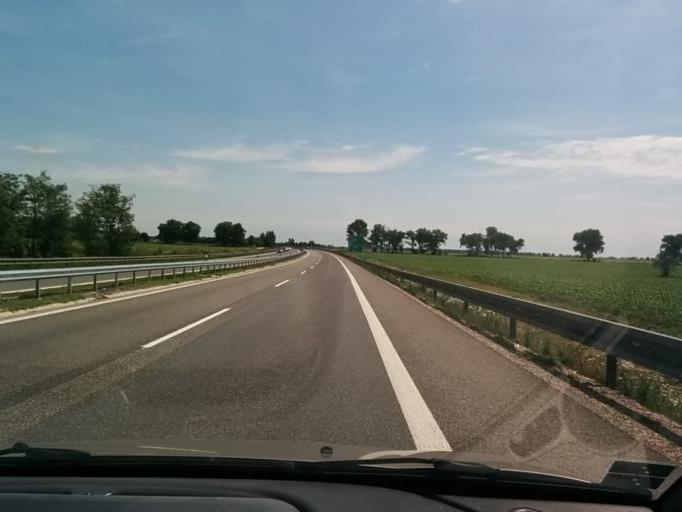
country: SK
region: Trnavsky
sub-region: Okres Galanta
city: Galanta
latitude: 48.2619
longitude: 17.7324
